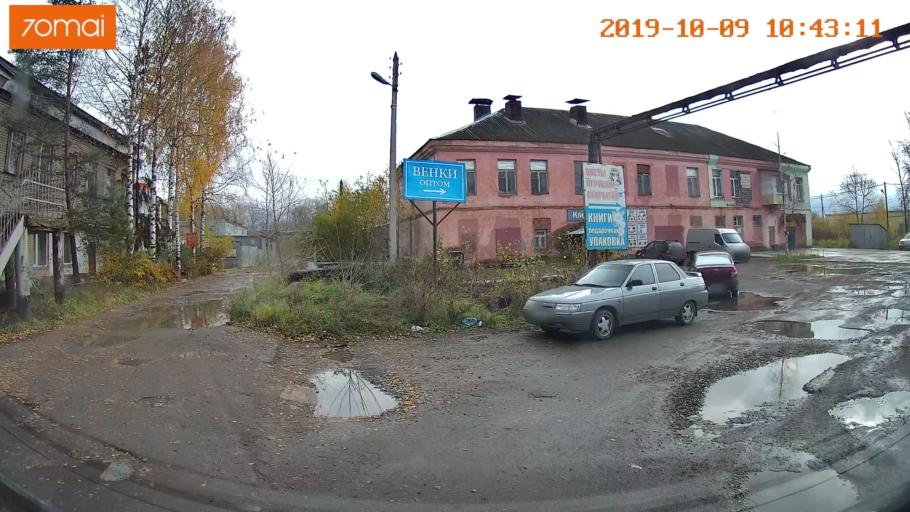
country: RU
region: Vologda
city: Vologda
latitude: 59.2371
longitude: 39.8154
